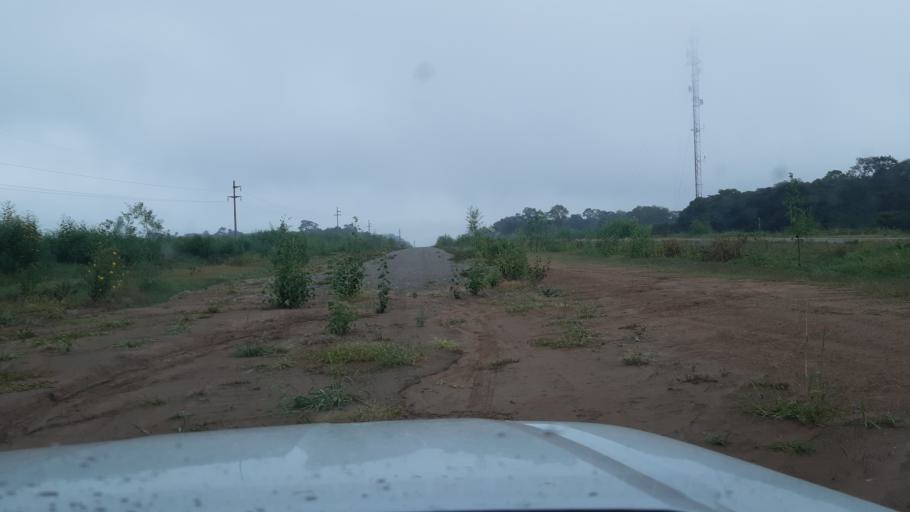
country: AR
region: Jujuy
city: La Mendieta
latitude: -24.3757
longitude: -65.0098
